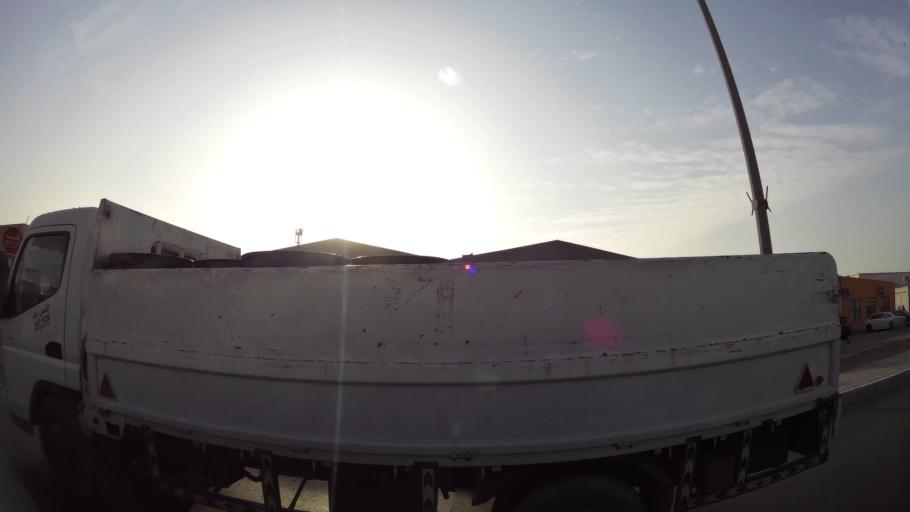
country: AE
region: Abu Dhabi
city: Abu Dhabi
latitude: 24.3754
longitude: 54.5107
